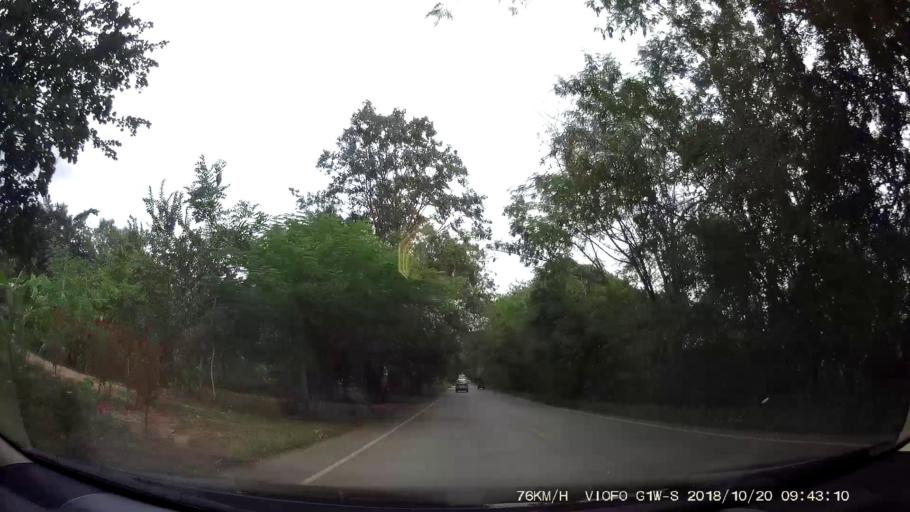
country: TH
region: Chaiyaphum
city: Khon San
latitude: 16.4709
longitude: 101.9492
